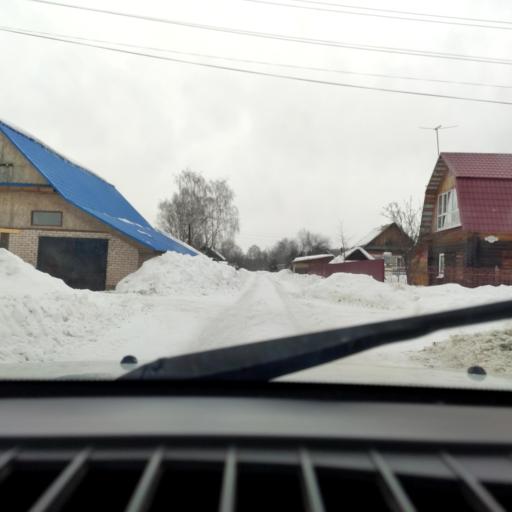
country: RU
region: Perm
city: Krasnokamsk
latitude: 58.0982
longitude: 55.8065
